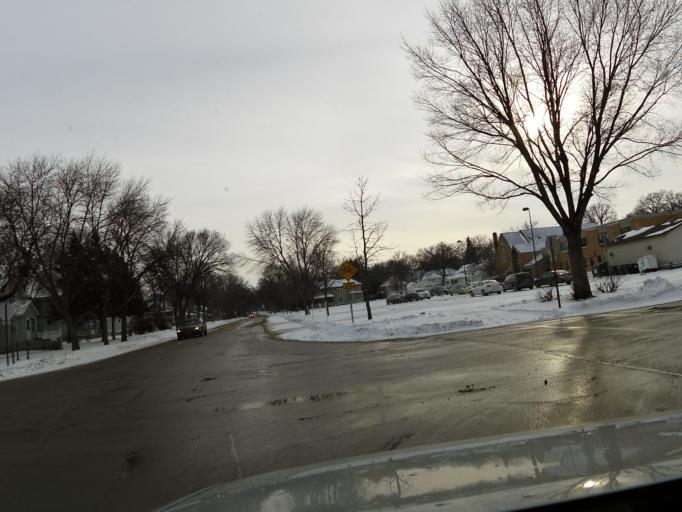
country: US
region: Minnesota
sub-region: McLeod County
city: Hutchinson
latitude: 44.8889
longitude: -94.3679
